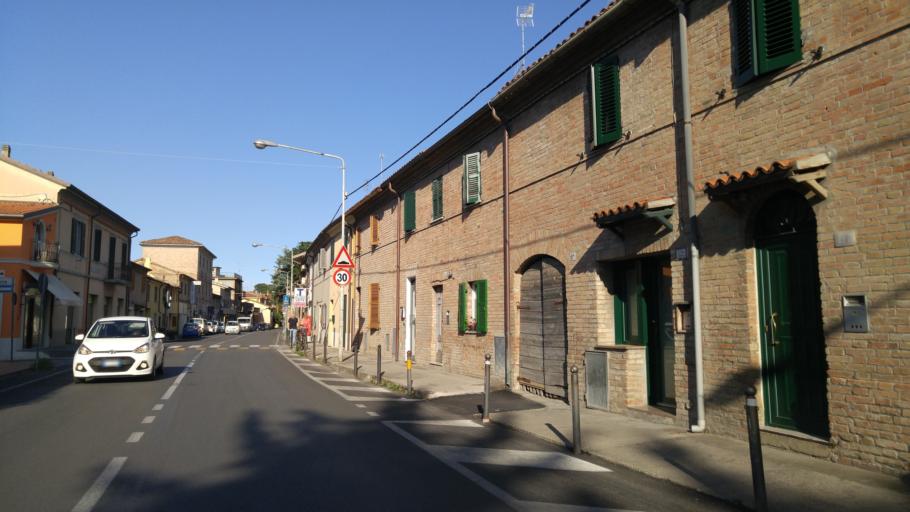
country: IT
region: The Marches
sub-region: Provincia di Pesaro e Urbino
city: Pesaro
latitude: 43.8830
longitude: 12.8700
